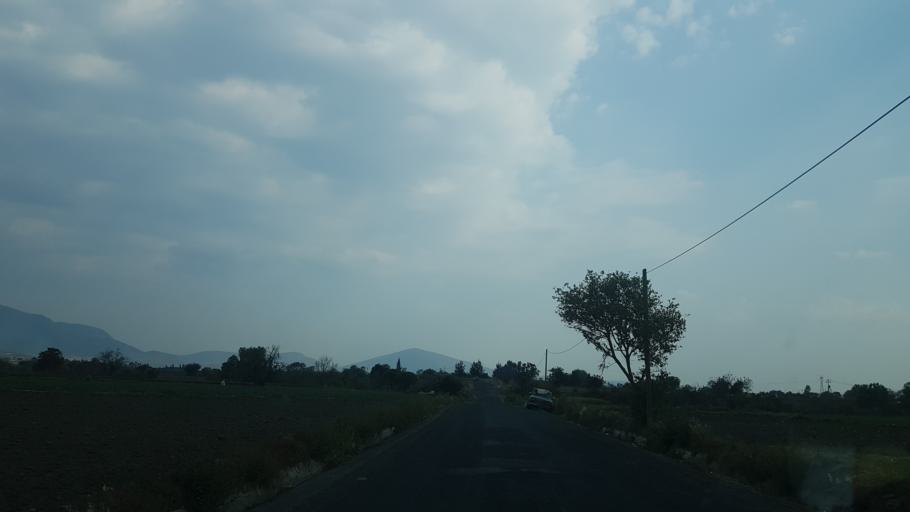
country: MX
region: Puebla
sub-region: Santa Isabel Cholula
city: Santa Ana Acozautla
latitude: 18.9615
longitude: -98.3954
